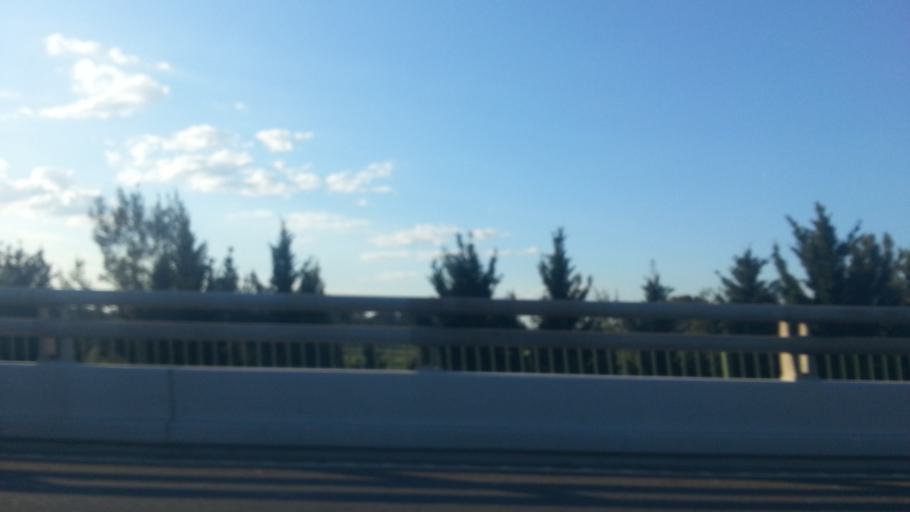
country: AU
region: New South Wales
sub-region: Camden
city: Camden South
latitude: -34.0683
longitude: 150.7063
